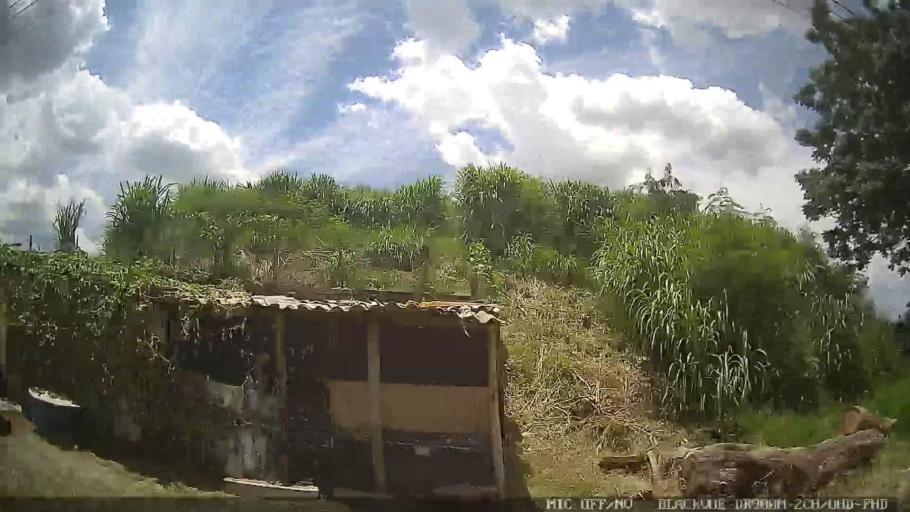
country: BR
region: Sao Paulo
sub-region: Atibaia
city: Atibaia
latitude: -23.1135
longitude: -46.5836
